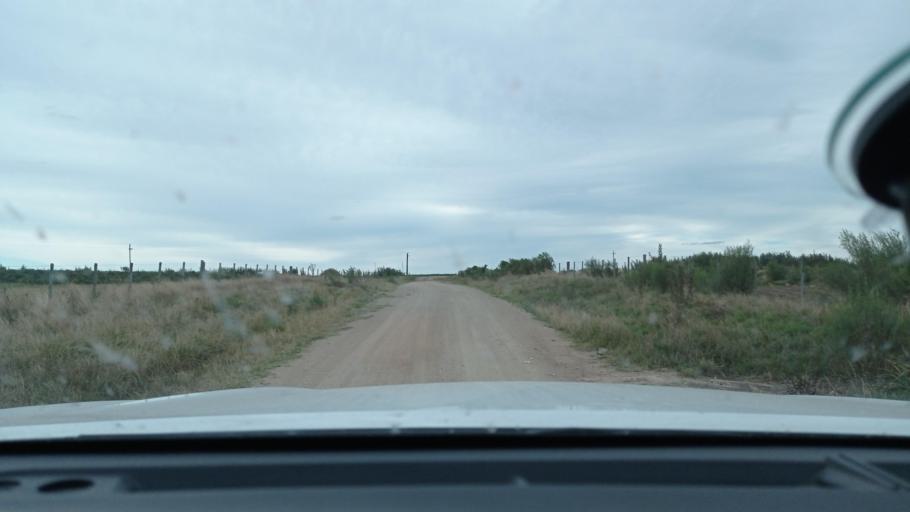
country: UY
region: Florida
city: Casupa
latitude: -34.1053
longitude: -55.7549
